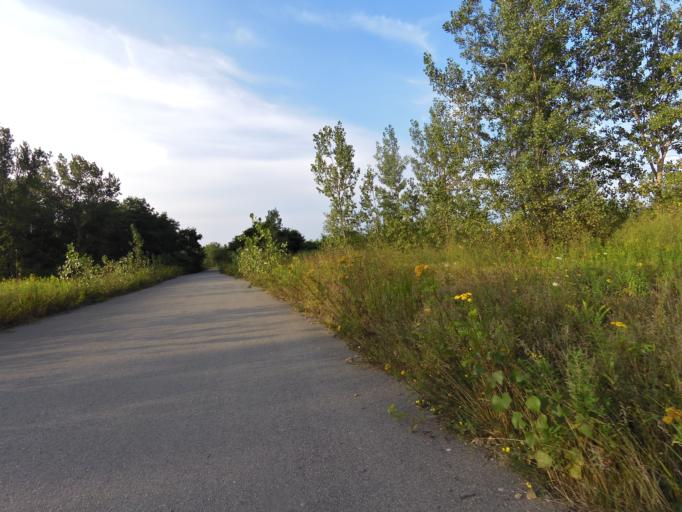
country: CA
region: Ontario
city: Toronto
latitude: 43.6158
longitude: -79.3430
